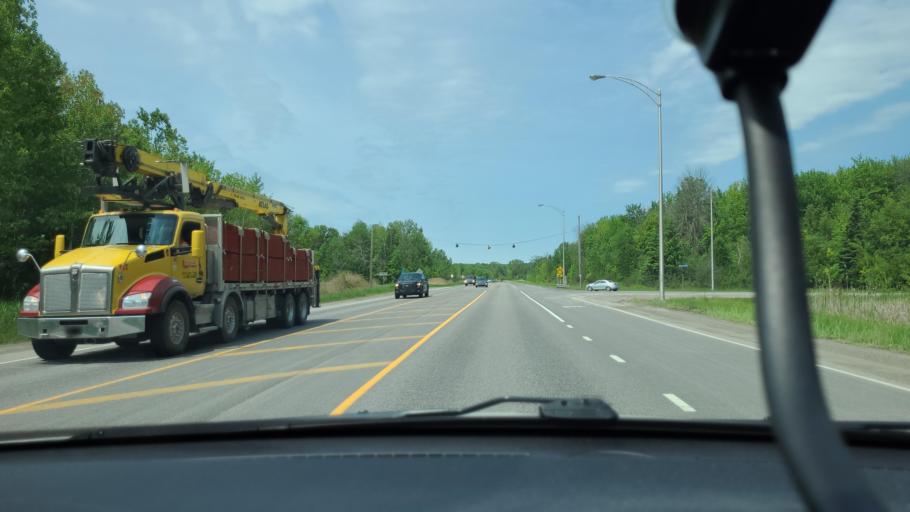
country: CA
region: Quebec
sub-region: Lanaudiere
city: Saint-Jacques
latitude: 45.9706
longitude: -73.5358
